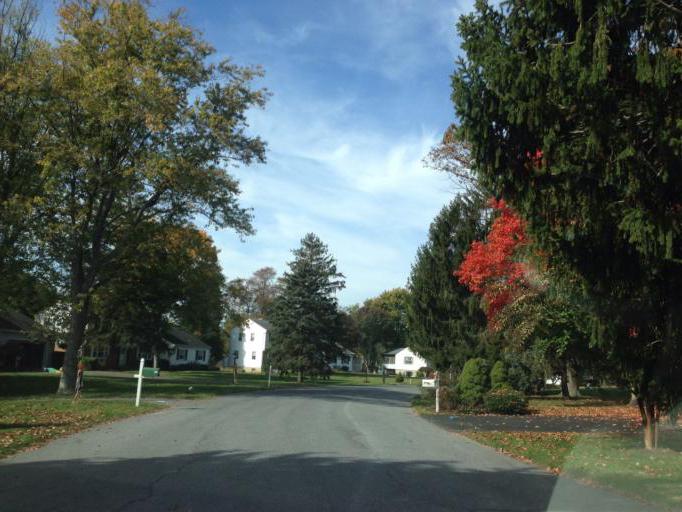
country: US
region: Maryland
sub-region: Howard County
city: Columbia
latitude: 39.2804
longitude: -76.8371
